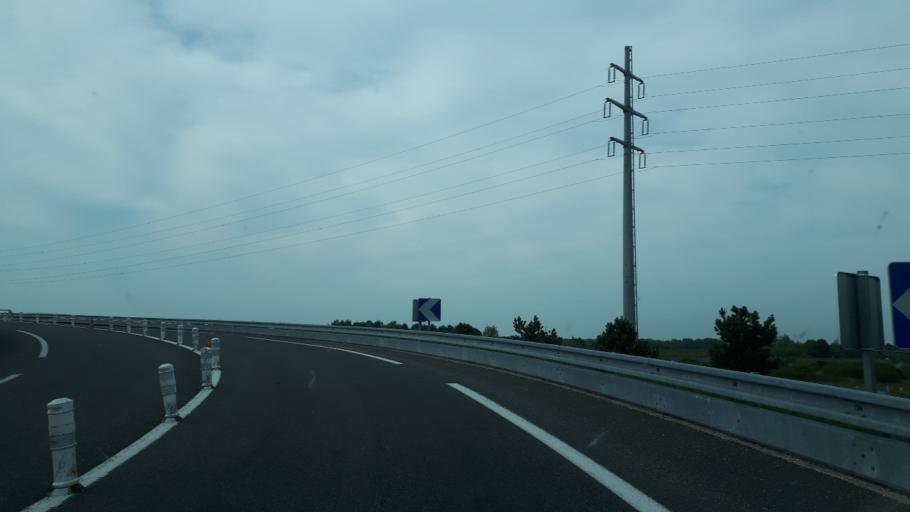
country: FR
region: Centre
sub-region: Departement du Loir-et-Cher
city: Chatillon-sur-Cher
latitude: 47.3295
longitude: 1.4999
